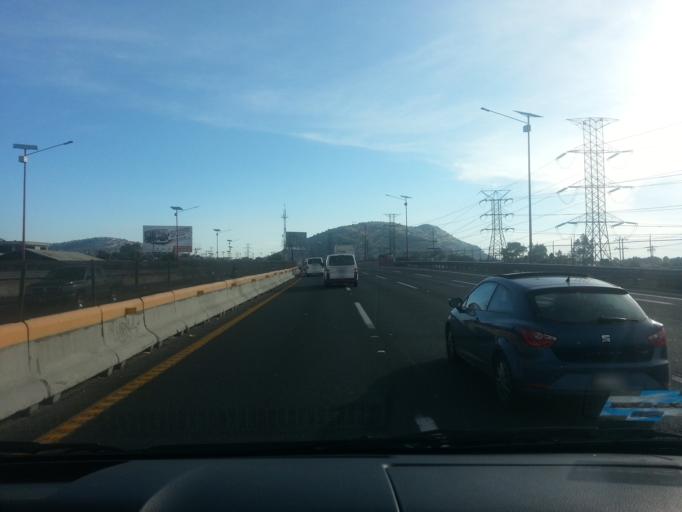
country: MX
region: Mexico
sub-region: Tlalnepantla de Baz
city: Puerto Escondido (Tepeolulco Puerto Escondido)
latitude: 19.5334
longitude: -99.0780
